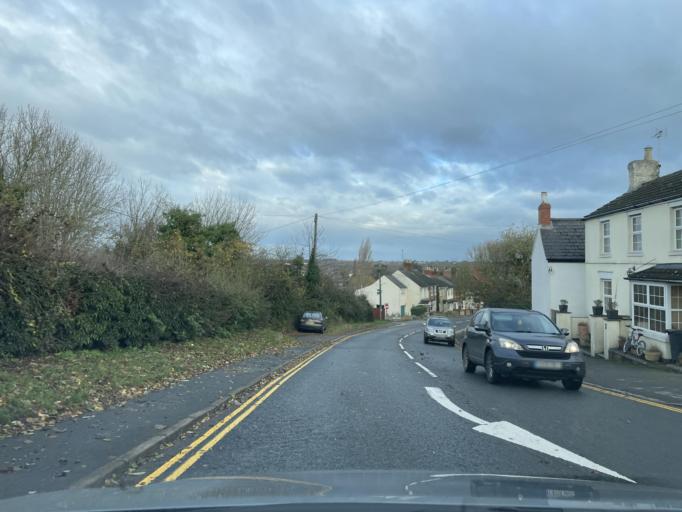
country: GB
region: England
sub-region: Borough of Swindon
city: Wroughton
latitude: 51.5219
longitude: -1.7994
